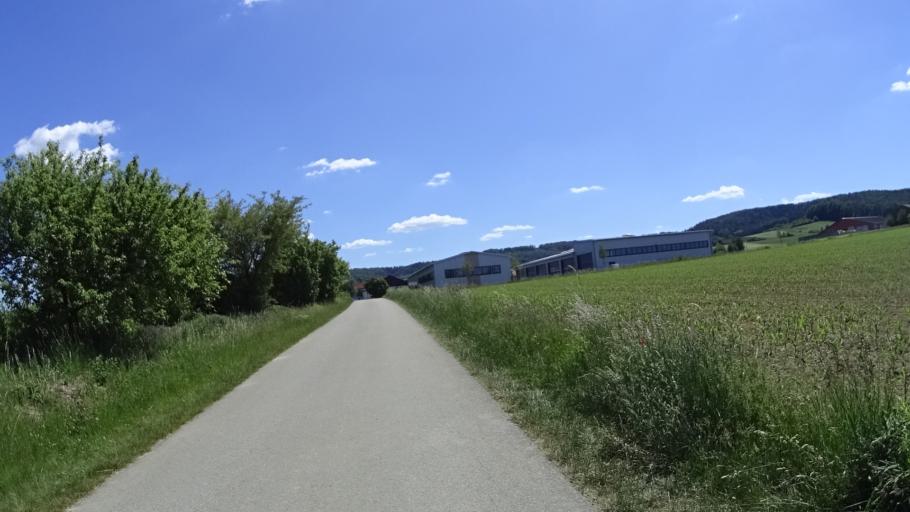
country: DE
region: Bavaria
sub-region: Regierungsbezirk Mittelfranken
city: Thalmassing
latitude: 49.0958
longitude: 11.2096
